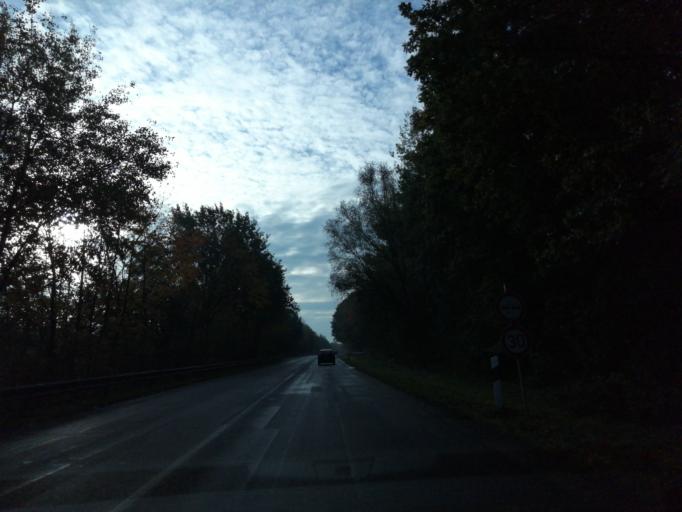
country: DE
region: Lower Saxony
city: Fedderwarden
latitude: 53.5959
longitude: 8.0525
